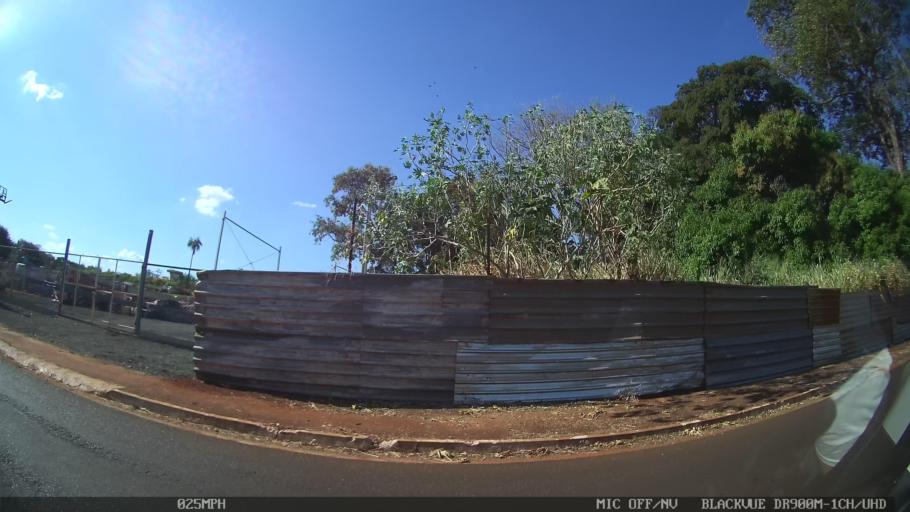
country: BR
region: Sao Paulo
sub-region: Ribeirao Preto
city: Ribeirao Preto
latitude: -21.1725
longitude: -47.7837
